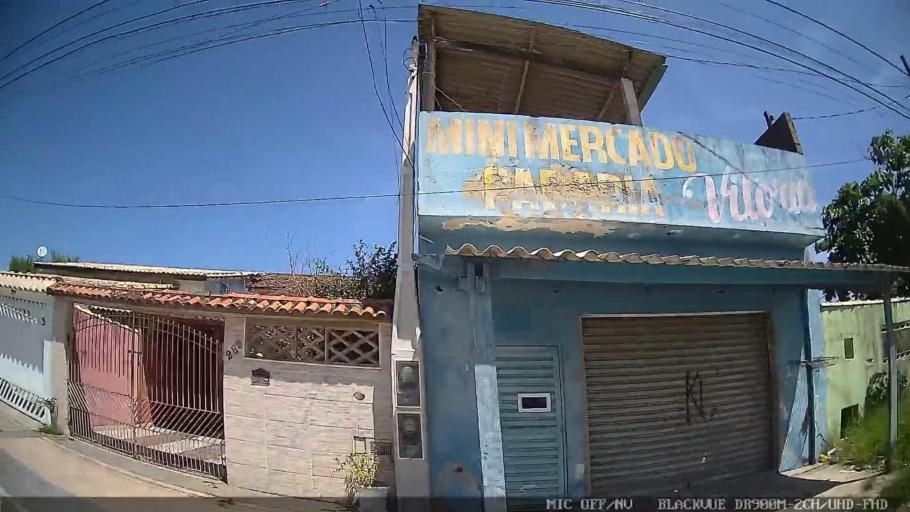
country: BR
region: Sao Paulo
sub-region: Peruibe
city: Peruibe
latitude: -24.3007
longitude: -46.9904
